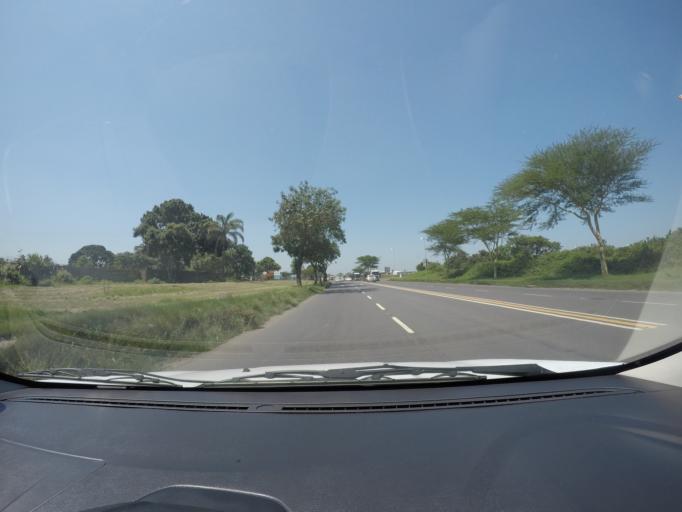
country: ZA
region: KwaZulu-Natal
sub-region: uThungulu District Municipality
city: Richards Bay
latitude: -28.7634
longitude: 32.0208
